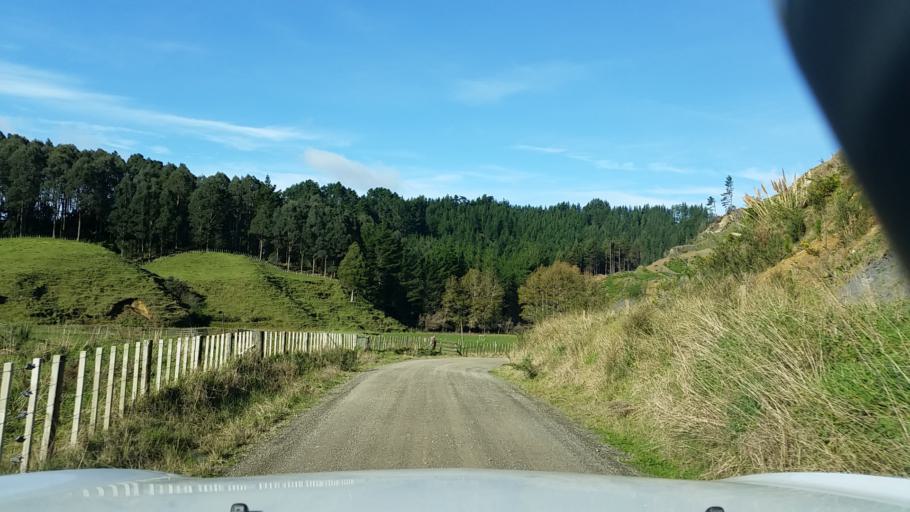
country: NZ
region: Taranaki
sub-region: New Plymouth District
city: Waitara
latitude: -38.9352
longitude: 174.5532
